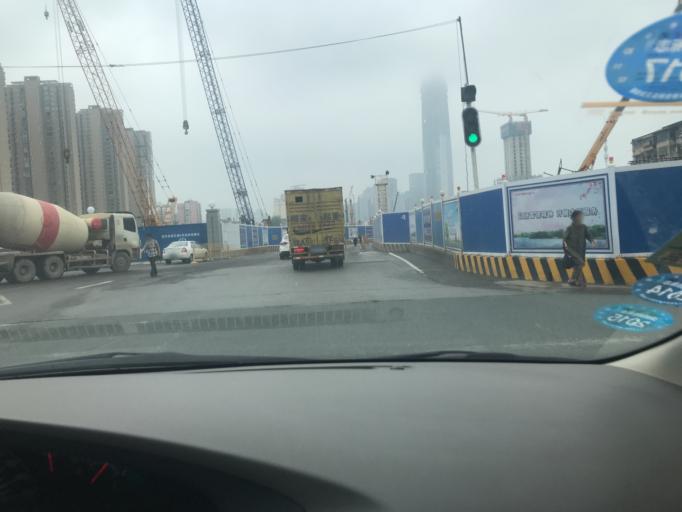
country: CN
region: Hubei
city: Jiang'an
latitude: 30.5949
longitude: 114.3301
